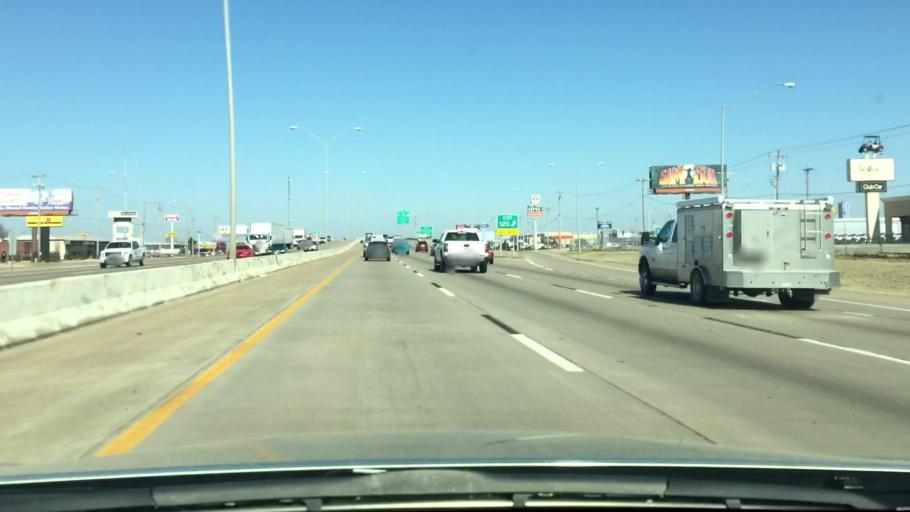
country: US
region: Oklahoma
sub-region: Cleveland County
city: Moore
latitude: 35.3738
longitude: -97.4949
